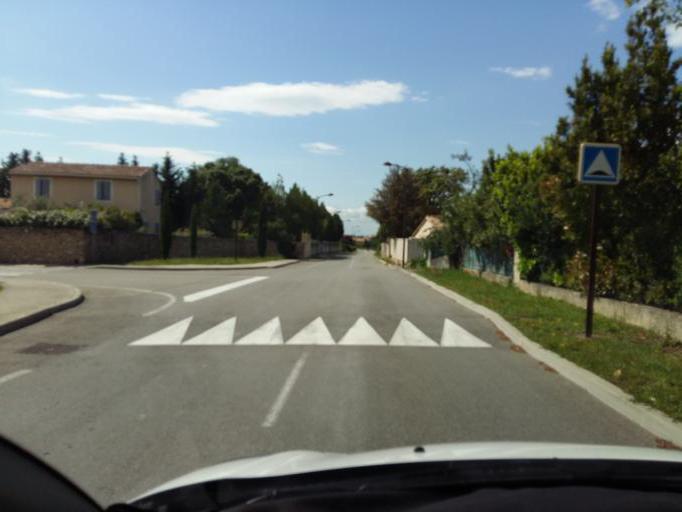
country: FR
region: Provence-Alpes-Cote d'Azur
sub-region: Departement du Vaucluse
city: Taillades
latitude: 43.8408
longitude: 5.0897
